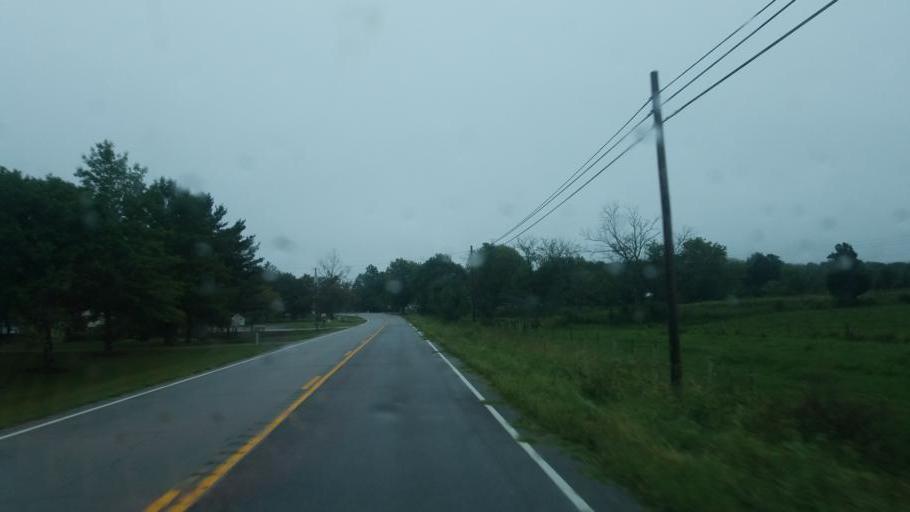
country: US
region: Kentucky
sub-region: Fleming County
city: Flemingsburg
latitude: 38.3847
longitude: -83.6573
